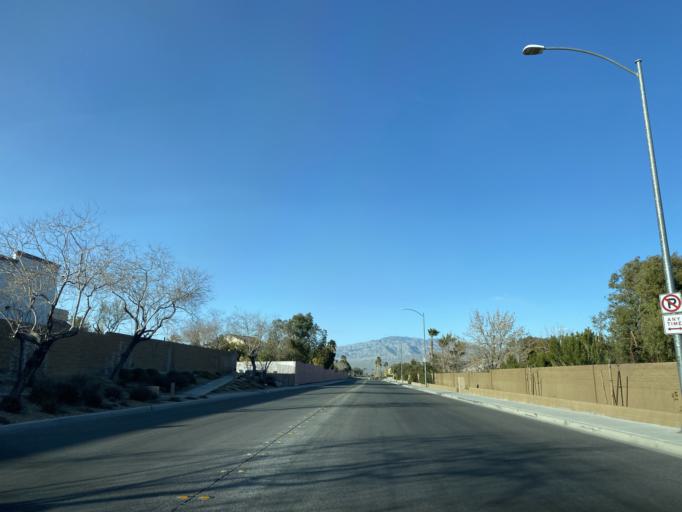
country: US
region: Nevada
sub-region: Clark County
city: Las Vegas
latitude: 36.3021
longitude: -115.2786
